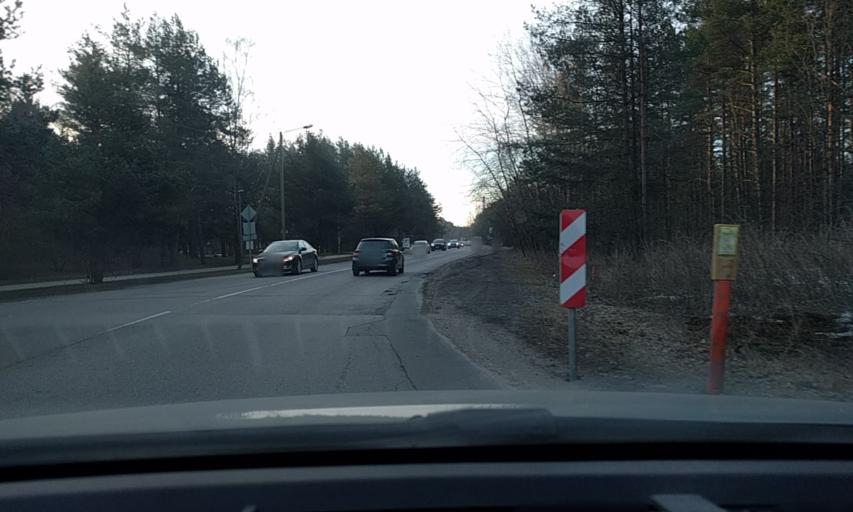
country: EE
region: Harju
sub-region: Tallinna linn
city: Kose
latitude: 59.4738
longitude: 24.8971
